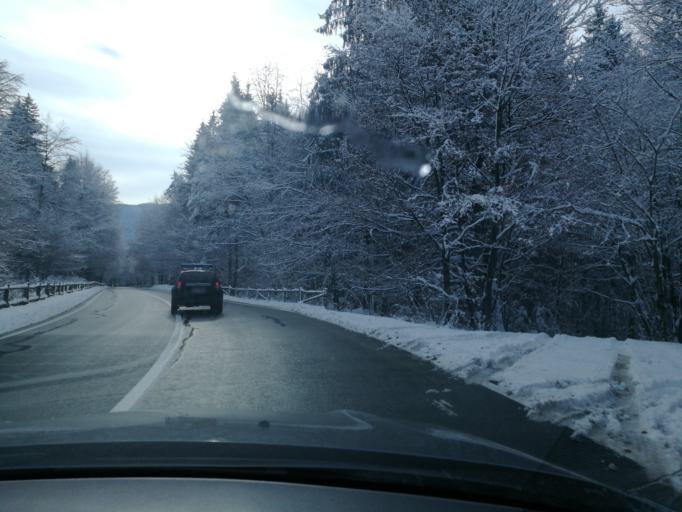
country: RO
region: Brasov
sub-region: Comuna Ghimbav
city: Ghimbav
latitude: 45.6200
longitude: 25.5428
